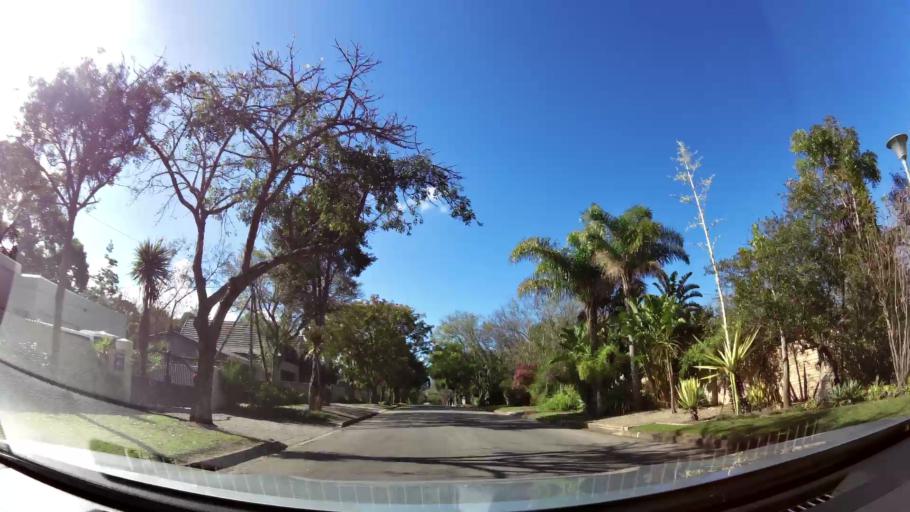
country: ZA
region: Western Cape
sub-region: Eden District Municipality
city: George
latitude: -33.9493
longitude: 22.4426
